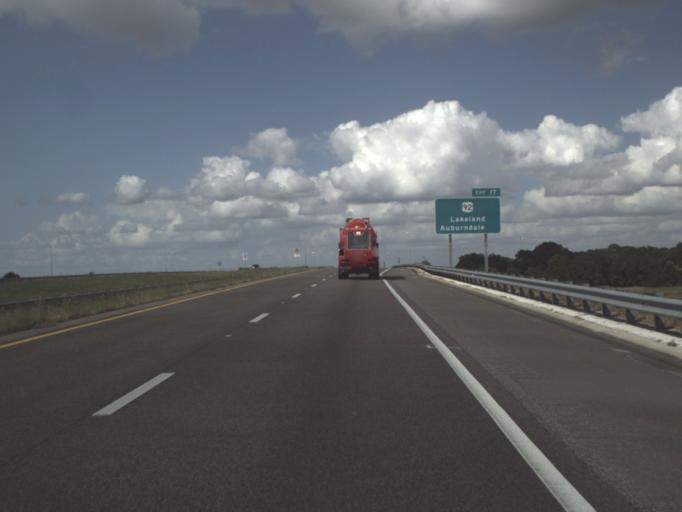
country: US
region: Florida
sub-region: Polk County
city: Fussels Corner
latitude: 28.0477
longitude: -81.8344
